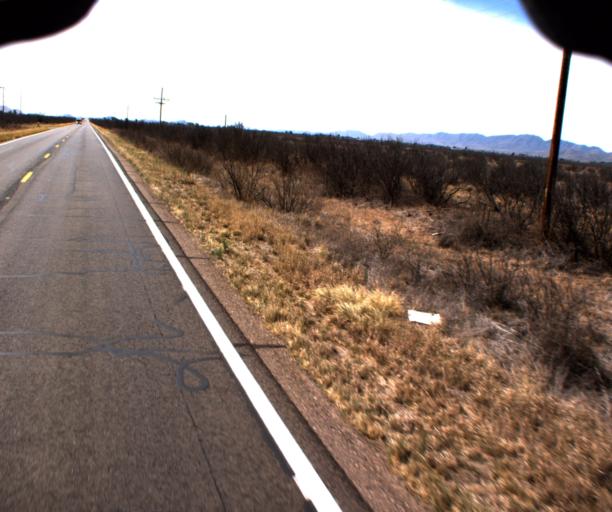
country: US
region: Arizona
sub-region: Cochise County
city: Willcox
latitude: 32.0263
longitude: -109.8741
